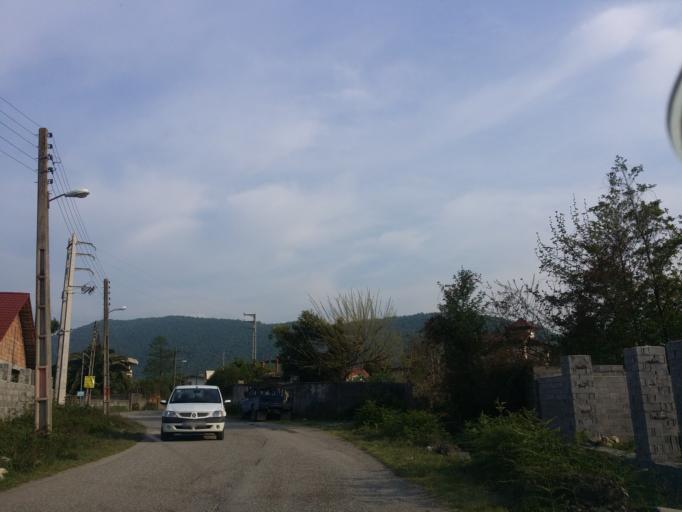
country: IR
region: Mazandaran
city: Chalus
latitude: 36.6592
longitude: 51.3670
